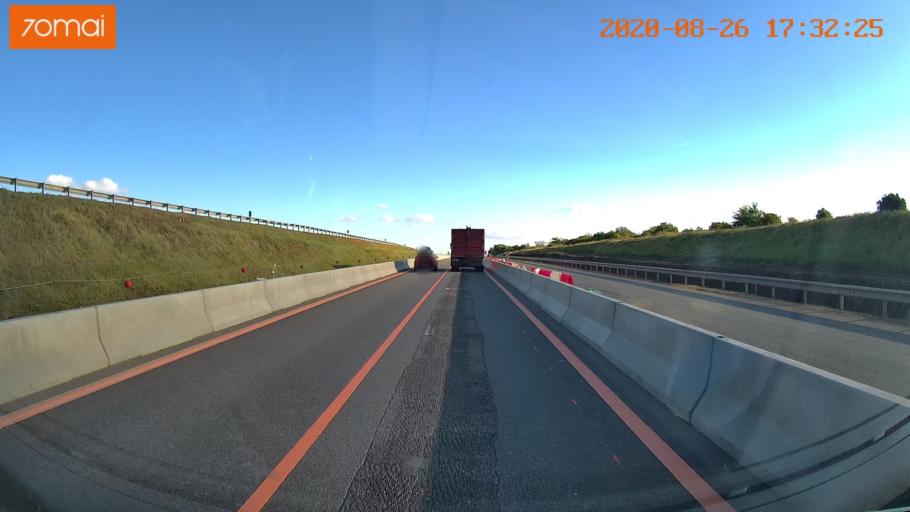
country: RU
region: Tula
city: Kazachka
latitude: 53.4223
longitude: 38.1809
